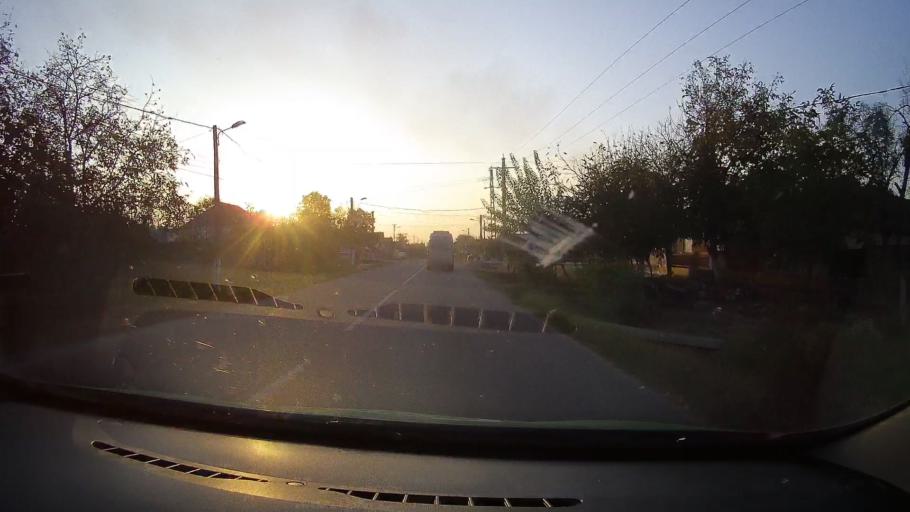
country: RO
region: Arad
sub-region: Comuna Sicula
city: Sicula
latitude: 46.4369
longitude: 21.7590
